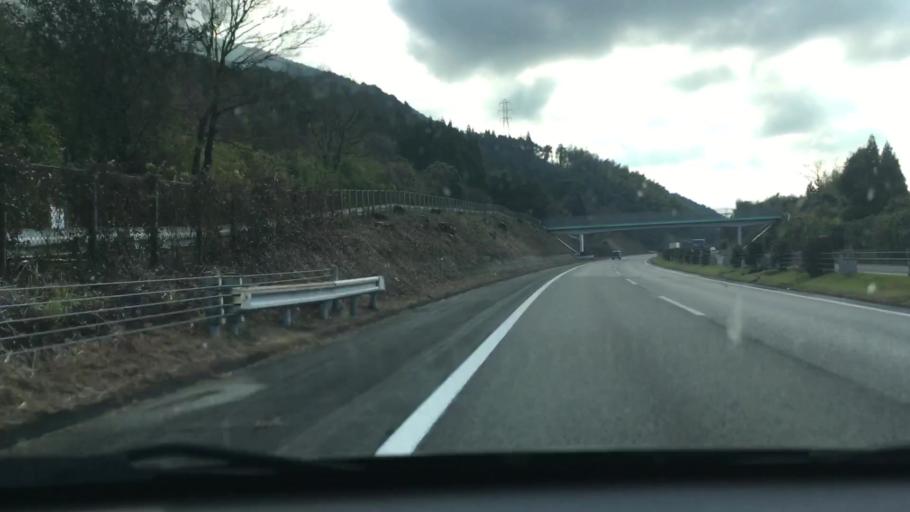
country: JP
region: Kumamoto
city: Yatsushiro
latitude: 32.5341
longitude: 130.6715
